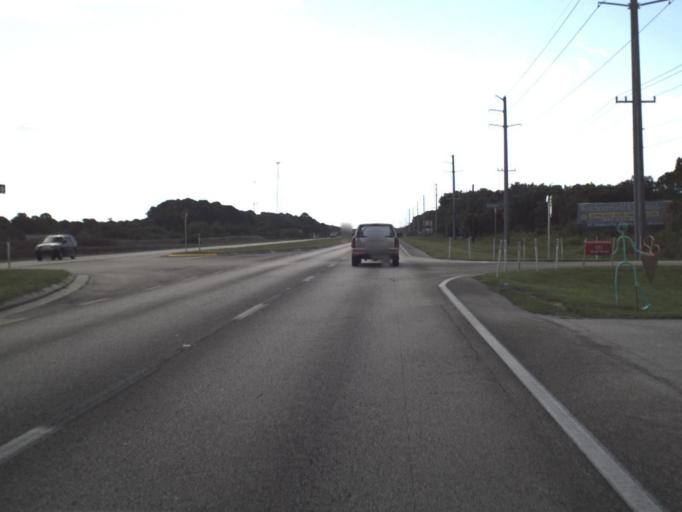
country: US
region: Florida
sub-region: Sarasota County
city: North Port
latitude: 27.0293
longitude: -82.2000
